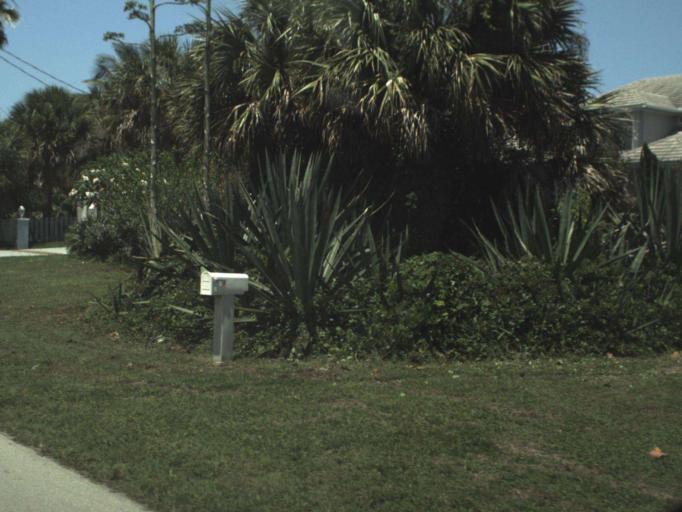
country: US
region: Florida
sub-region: Brevard County
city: Micco
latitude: 27.9482
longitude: -80.4978
